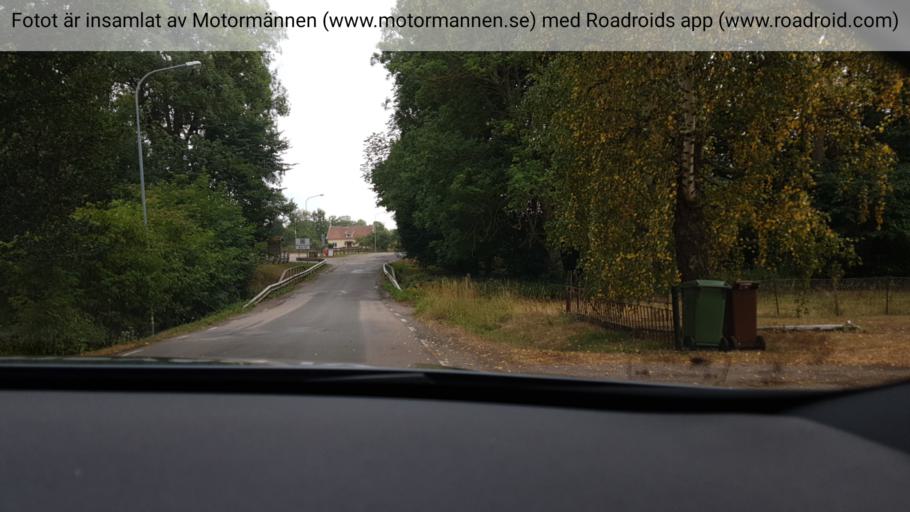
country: SE
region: Vaestra Goetaland
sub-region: Falkopings Kommun
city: Akarp
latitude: 58.1793
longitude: 13.6867
